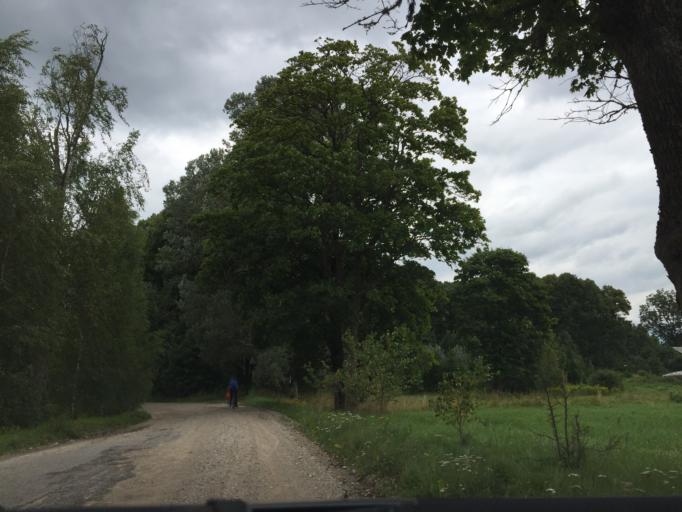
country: LV
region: Seja
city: Loja
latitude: 57.1455
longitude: 24.6626
